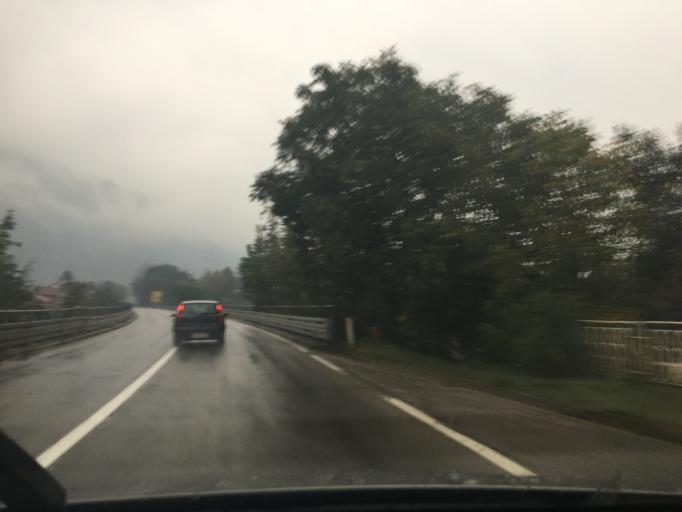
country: RS
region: Central Serbia
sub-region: Pcinjski Okrug
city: Vladicin Han
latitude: 42.8282
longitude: 22.1317
